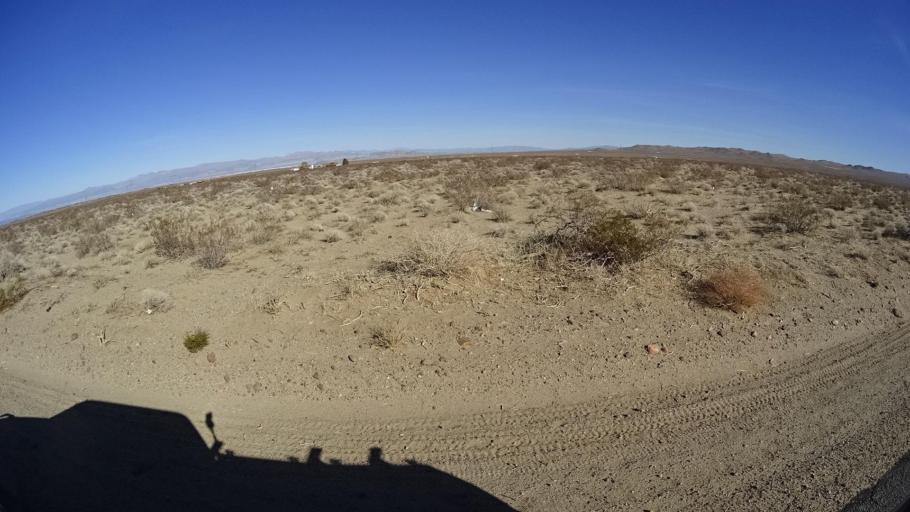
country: US
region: California
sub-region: Kern County
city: China Lake Acres
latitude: 35.5696
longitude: -117.7804
